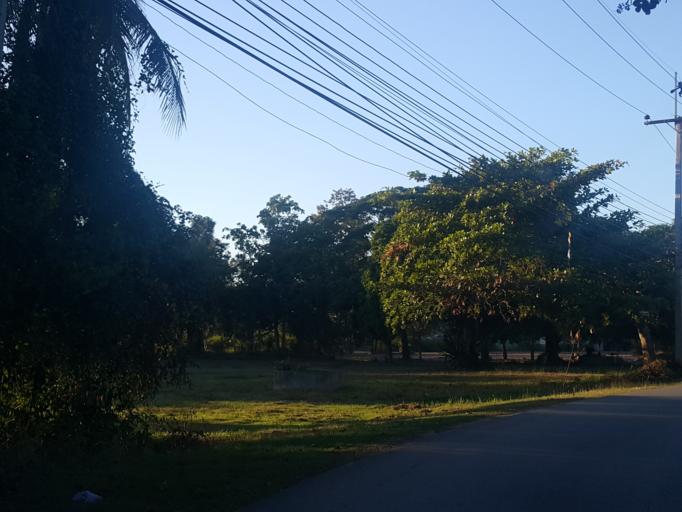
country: TH
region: Chiang Mai
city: San Sai
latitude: 18.8711
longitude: 99.1509
